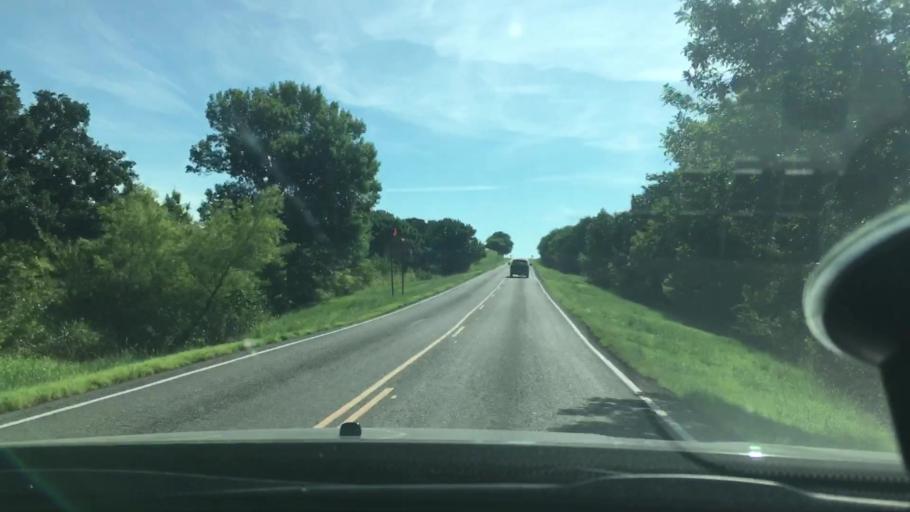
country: US
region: Oklahoma
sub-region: Carter County
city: Lone Grove
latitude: 34.3327
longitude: -97.2281
